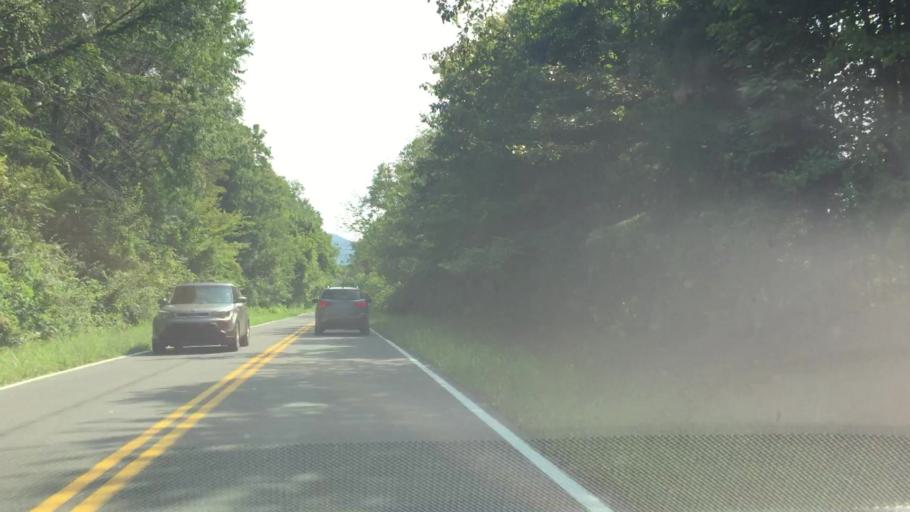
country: US
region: Virginia
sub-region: Pulaski County
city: Pulaski
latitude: 36.9869
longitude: -80.8210
